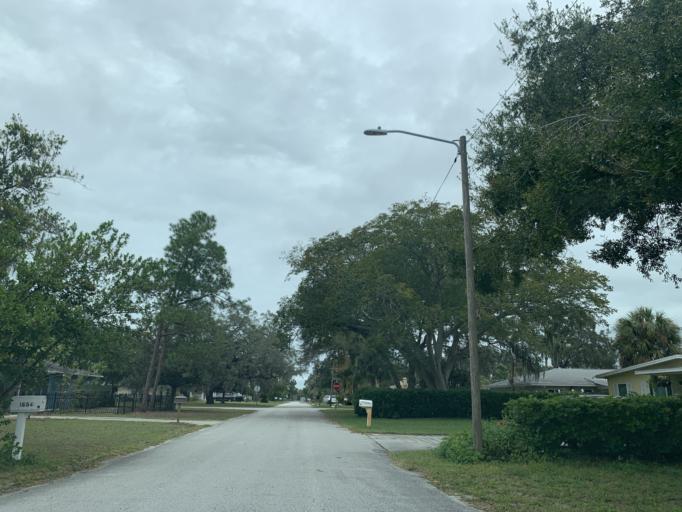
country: US
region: Florida
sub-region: Pinellas County
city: Belleair
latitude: 27.9364
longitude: -82.7844
